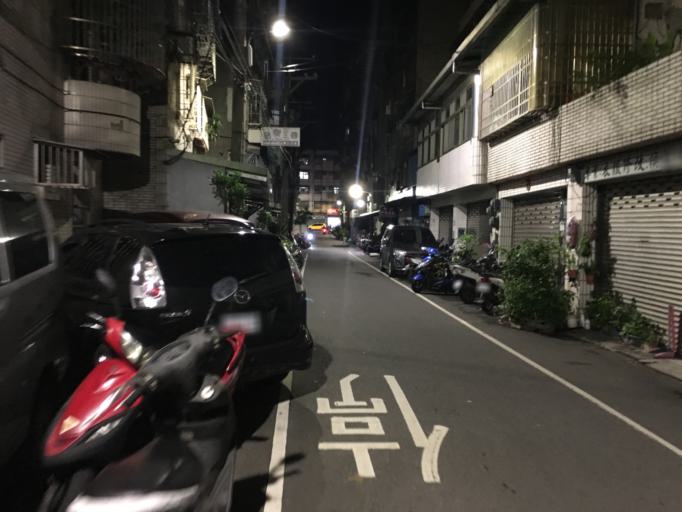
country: TW
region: Taipei
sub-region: Taipei
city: Banqiao
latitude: 24.9783
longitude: 121.4168
